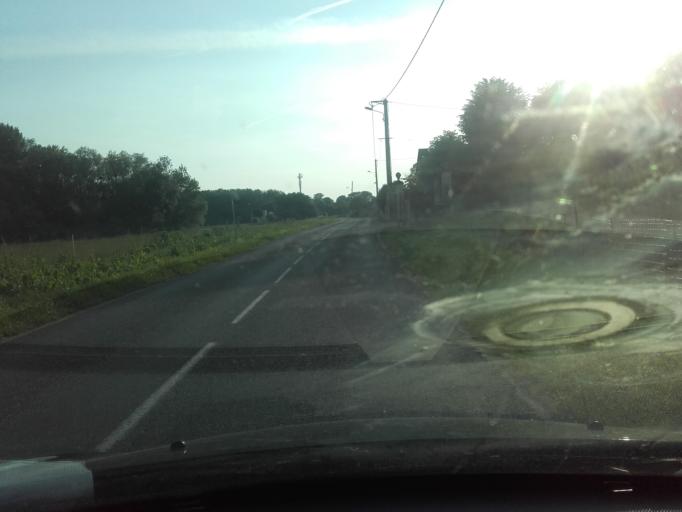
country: FR
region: Centre
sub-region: Departement d'Indre-et-Loire
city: Vernou-sur-Brenne
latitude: 47.4139
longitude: 0.8543
